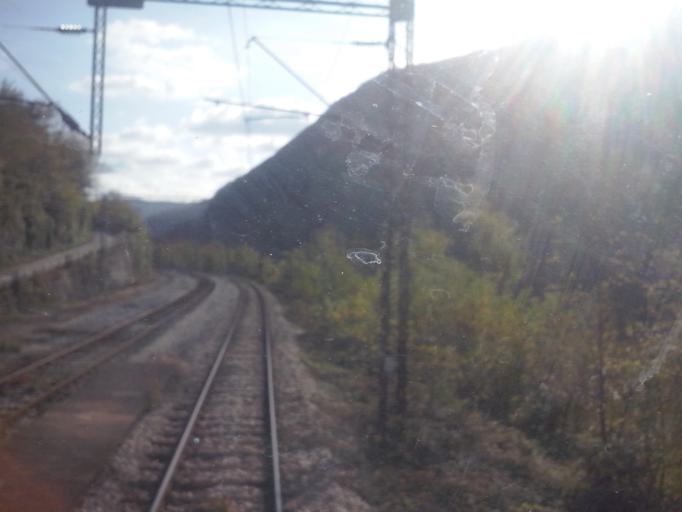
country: RS
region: Central Serbia
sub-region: Kolubarski Okrug
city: Valjevo
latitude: 44.1559
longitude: 19.8874
